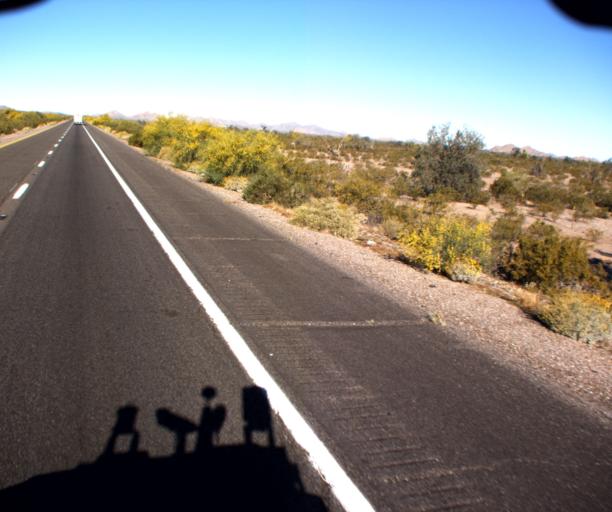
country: US
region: Arizona
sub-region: Pinal County
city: Maricopa
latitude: 32.8304
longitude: -112.0189
